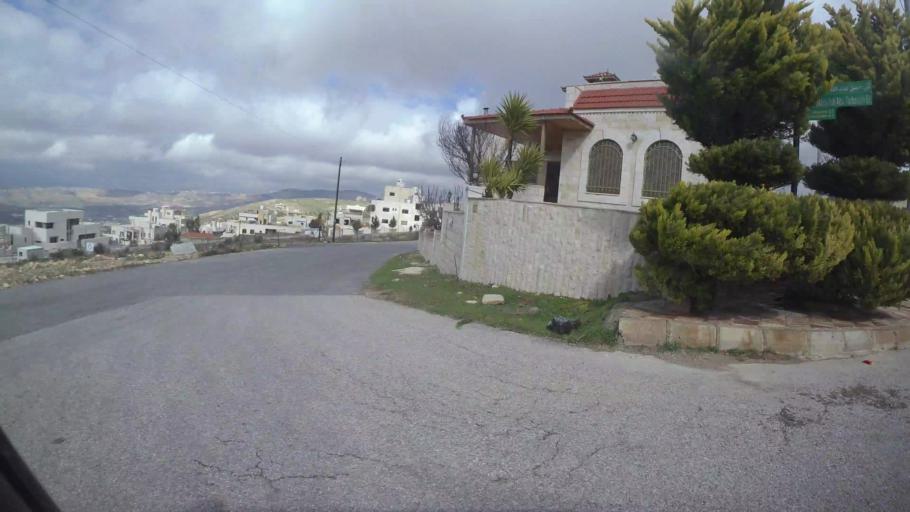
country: JO
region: Amman
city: Al Jubayhah
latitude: 32.0701
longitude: 35.8789
